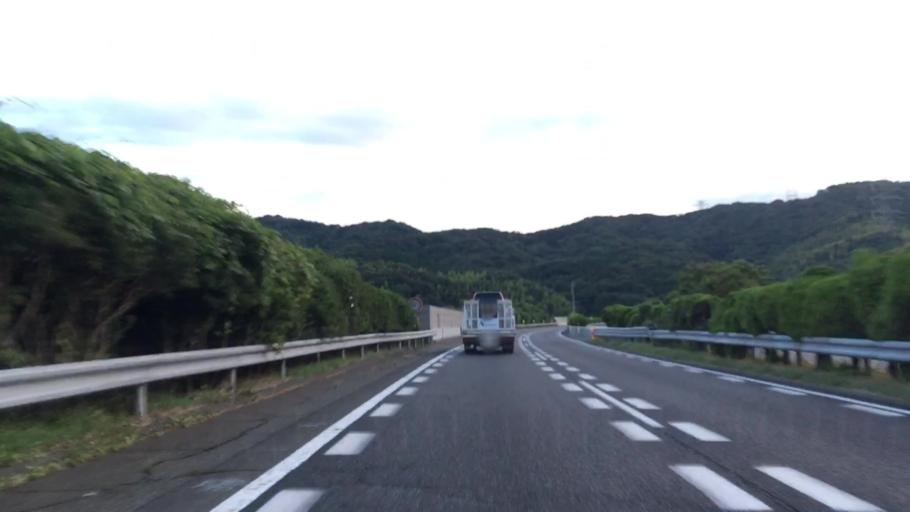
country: JP
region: Yamaguchi
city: Shimonoseki
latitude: 33.9312
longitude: 130.9952
